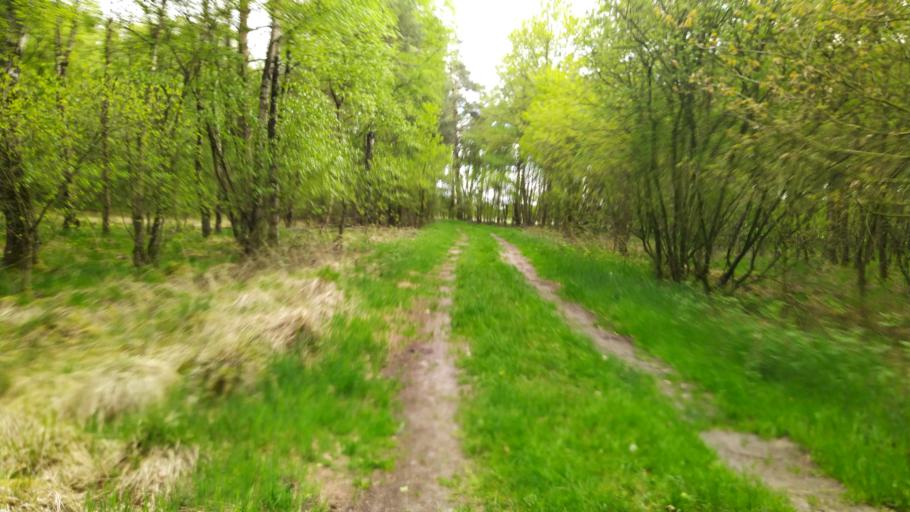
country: DE
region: Lower Saxony
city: Brest
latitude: 53.4309
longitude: 9.3905
